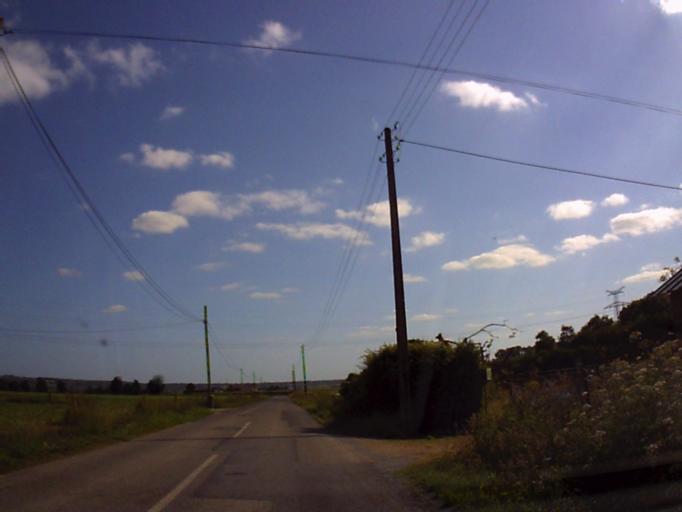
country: FR
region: Brittany
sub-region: Departement d'Ille-et-Vilaine
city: Iffendic
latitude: 48.1527
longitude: -2.0144
